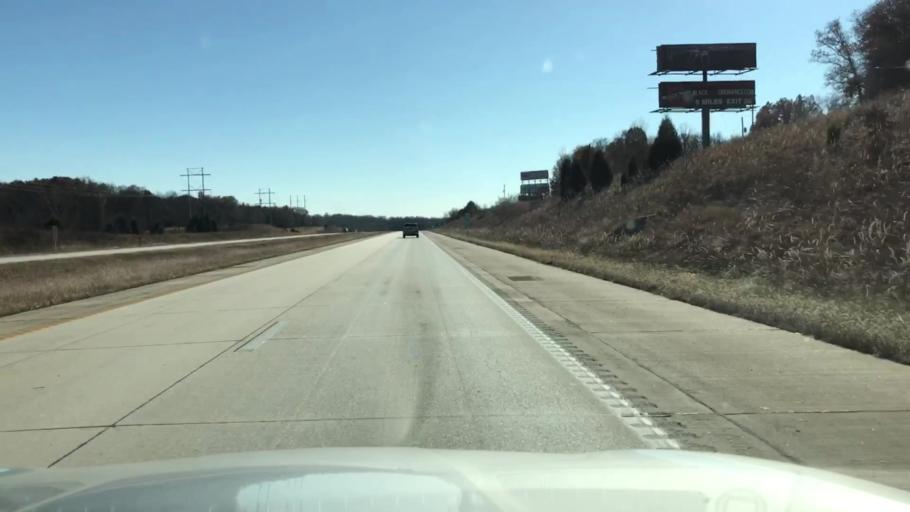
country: US
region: Missouri
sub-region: Jasper County
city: Duquesne
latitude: 37.0067
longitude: -94.4308
